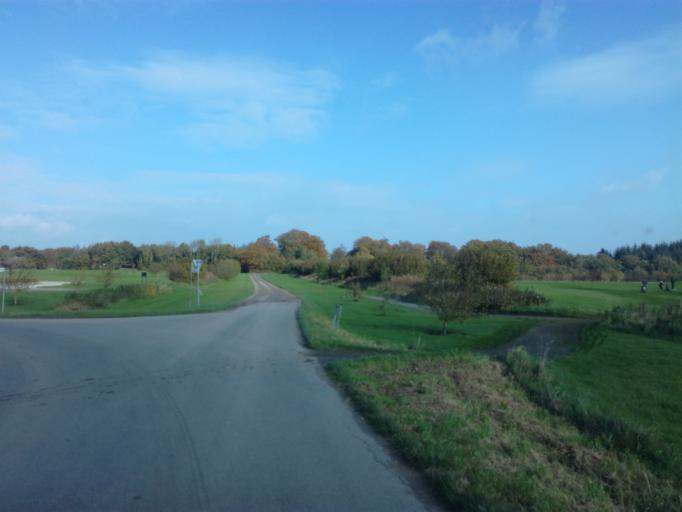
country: DK
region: South Denmark
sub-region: Vejle Kommune
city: Brejning
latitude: 55.6559
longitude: 9.6857
